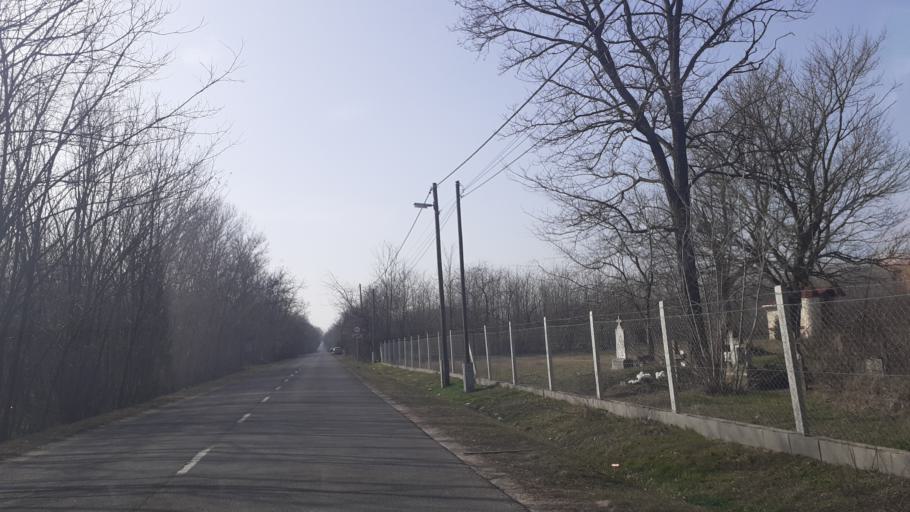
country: HU
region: Pest
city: Orkeny
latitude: 47.1222
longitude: 19.4190
